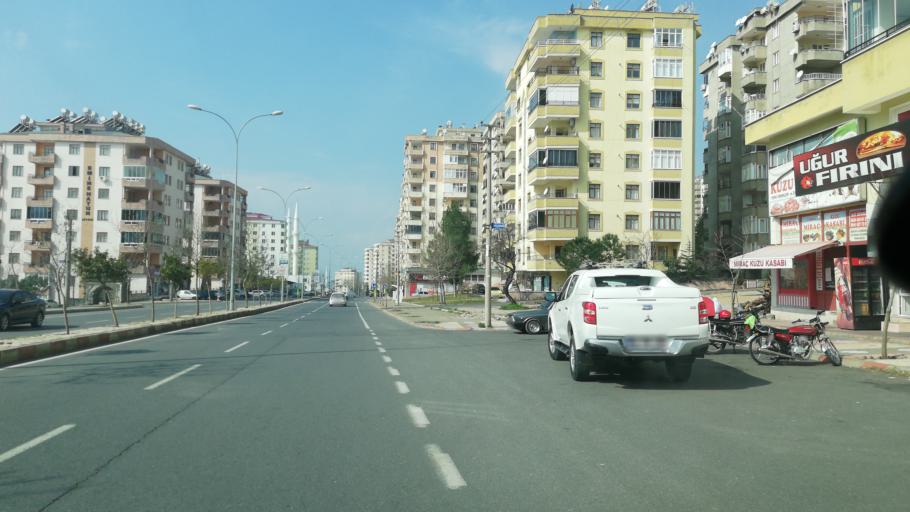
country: TR
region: Kahramanmaras
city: Kahramanmaras
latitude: 37.5867
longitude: 36.8832
